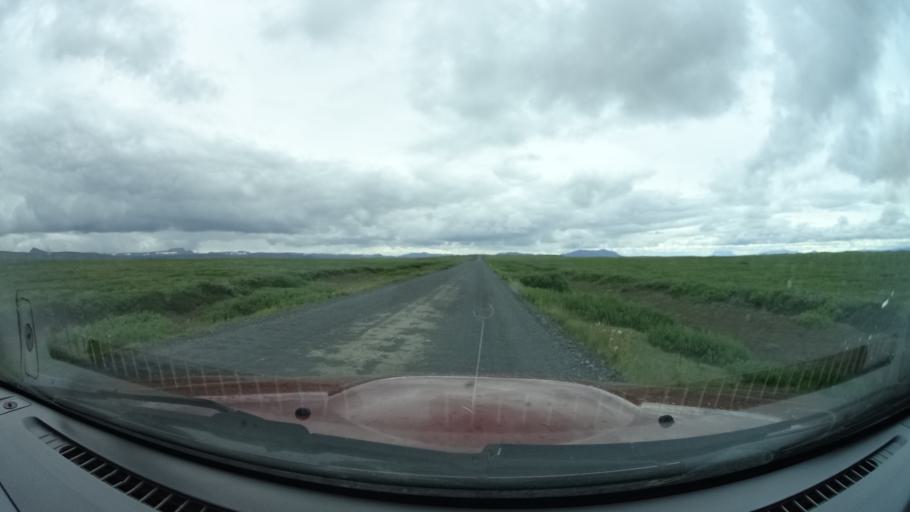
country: IS
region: Northeast
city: Laugar
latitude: 65.6869
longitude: -16.1811
